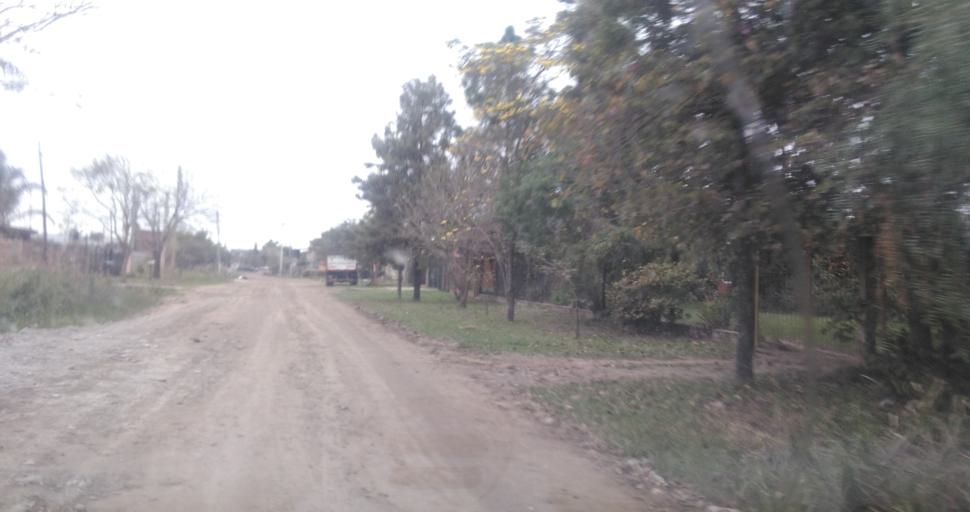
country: AR
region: Chaco
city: Fontana
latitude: -27.4354
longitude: -59.0204
